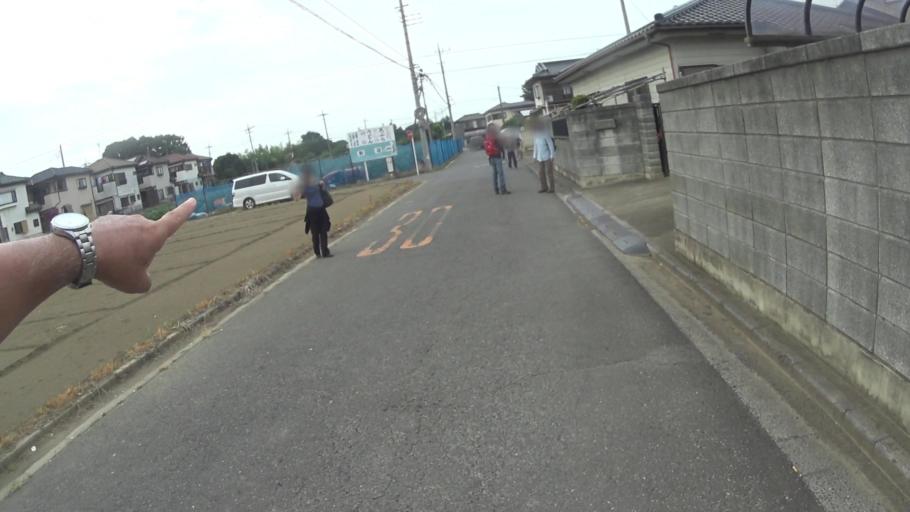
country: JP
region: Saitama
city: Okegawa
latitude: 35.9604
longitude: 139.5457
